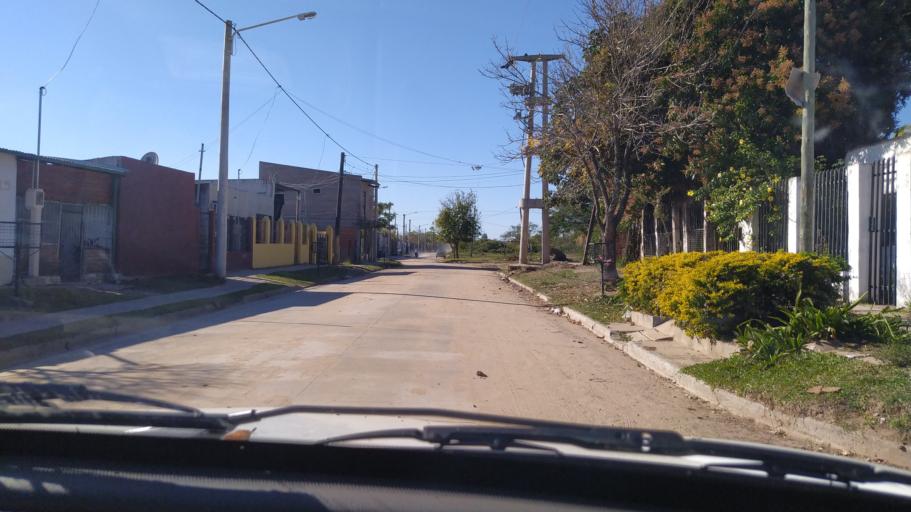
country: AR
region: Corrientes
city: Corrientes
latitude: -27.4999
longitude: -58.8067
